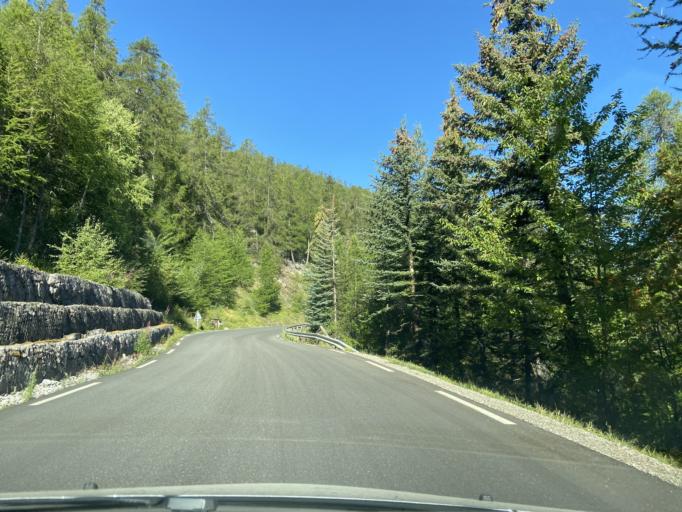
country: FR
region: Provence-Alpes-Cote d'Azur
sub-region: Departement des Hautes-Alpes
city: Guillestre
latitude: 44.6347
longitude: 6.6305
